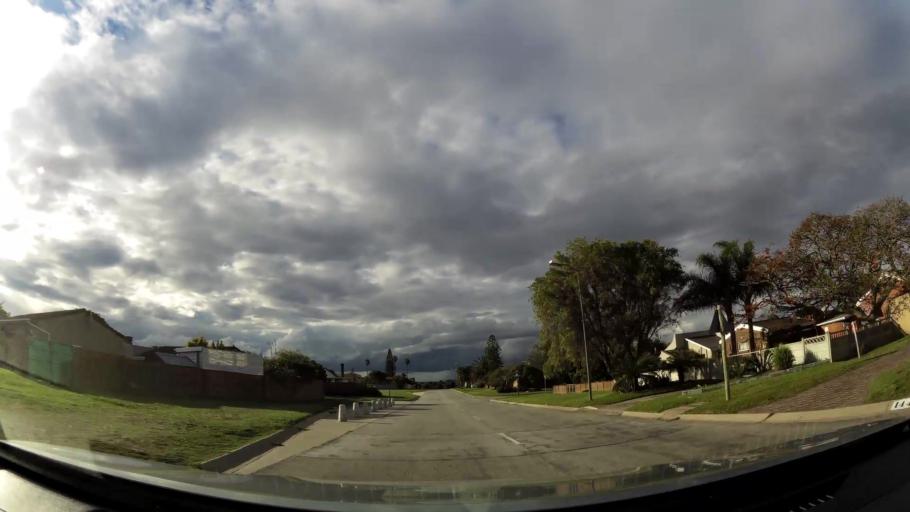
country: ZA
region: Eastern Cape
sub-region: Nelson Mandela Bay Metropolitan Municipality
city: Port Elizabeth
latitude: -33.9575
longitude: 25.4799
